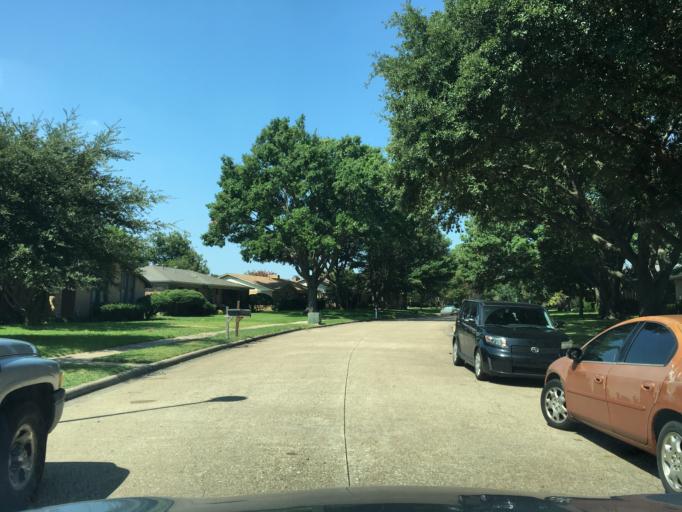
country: US
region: Texas
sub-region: Dallas County
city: Garland
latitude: 32.9363
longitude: -96.6490
